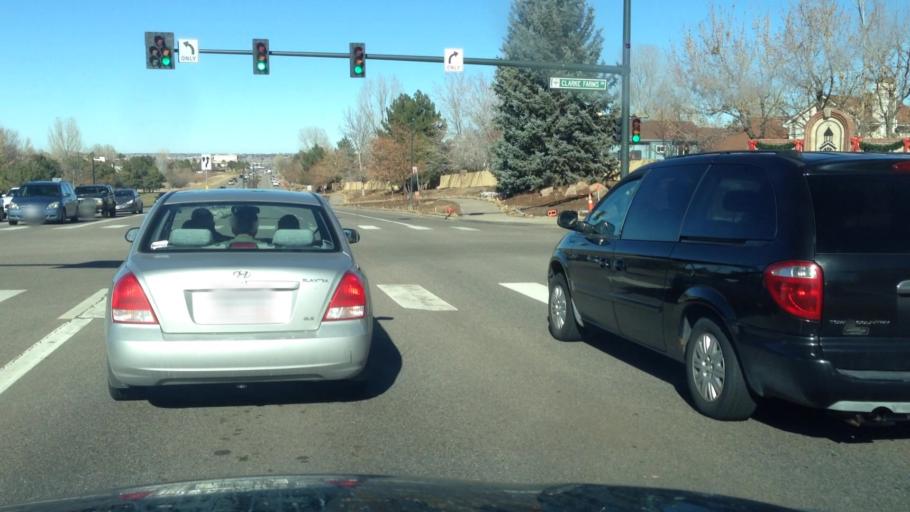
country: US
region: Colorado
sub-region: Douglas County
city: Stonegate
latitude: 39.5238
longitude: -104.7934
